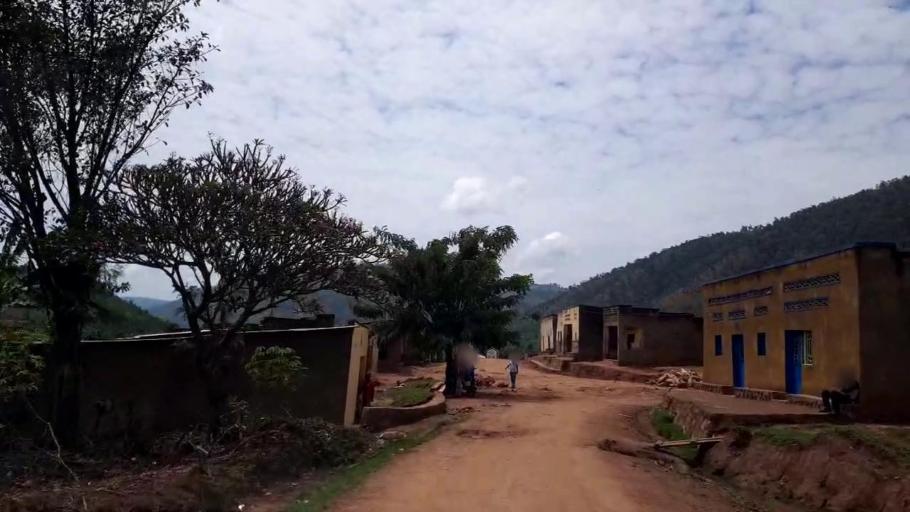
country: RW
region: Northern Province
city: Byumba
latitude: -1.4974
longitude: 30.1943
